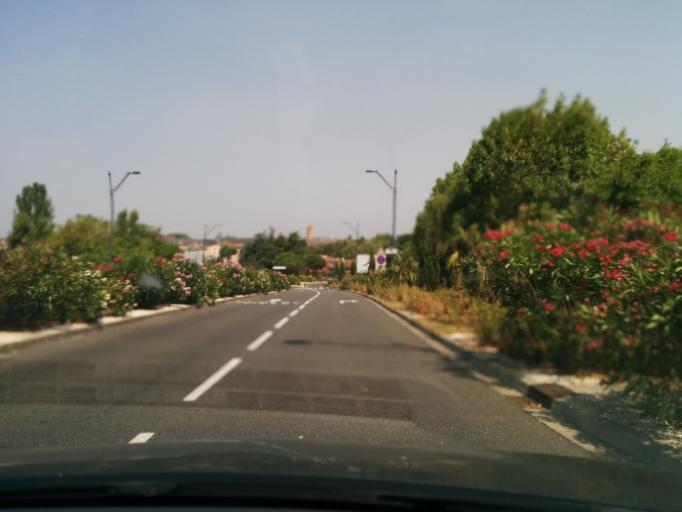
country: FR
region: Midi-Pyrenees
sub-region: Departement du Tarn
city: Albi
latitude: 43.9164
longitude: 2.1535
